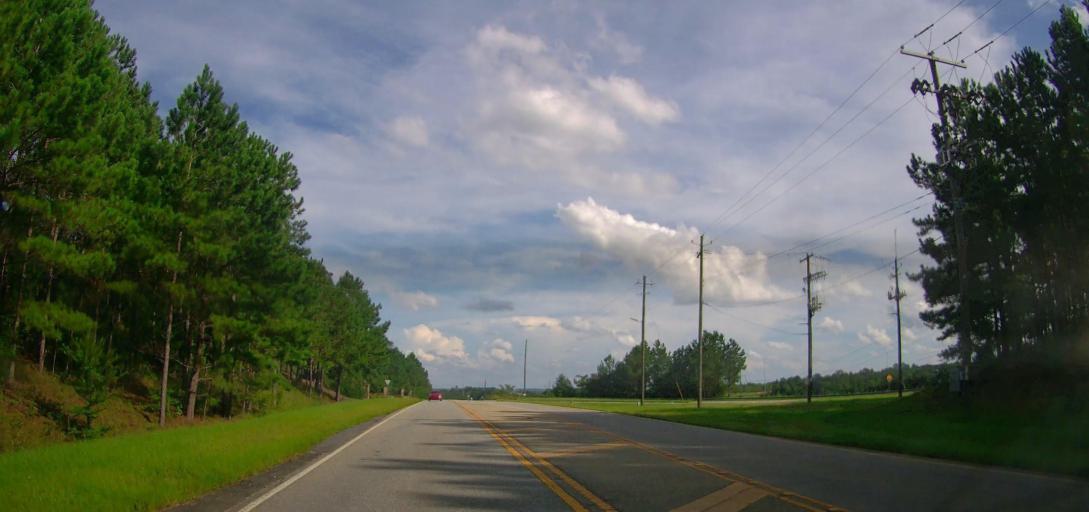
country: US
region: Alabama
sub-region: Russell County
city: Phenix City
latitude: 32.5117
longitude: -85.0084
